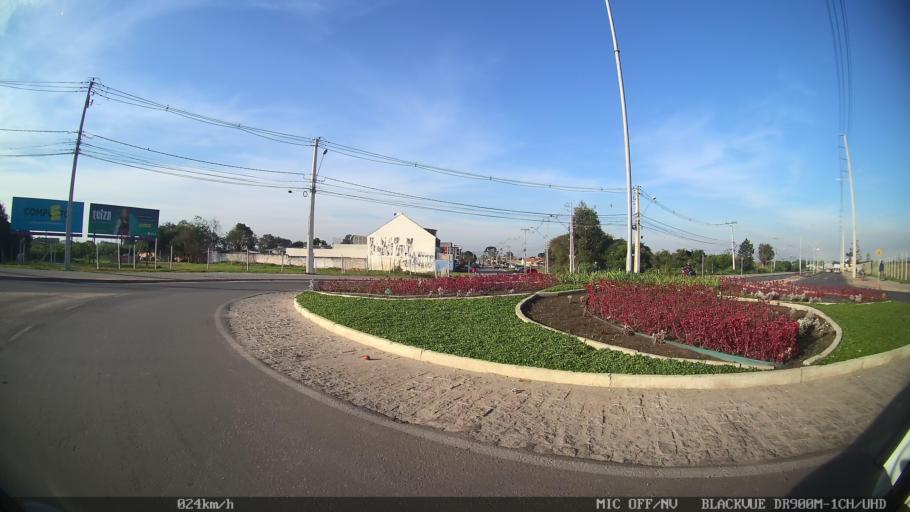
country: BR
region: Parana
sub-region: Pinhais
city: Pinhais
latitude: -25.4547
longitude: -49.1707
